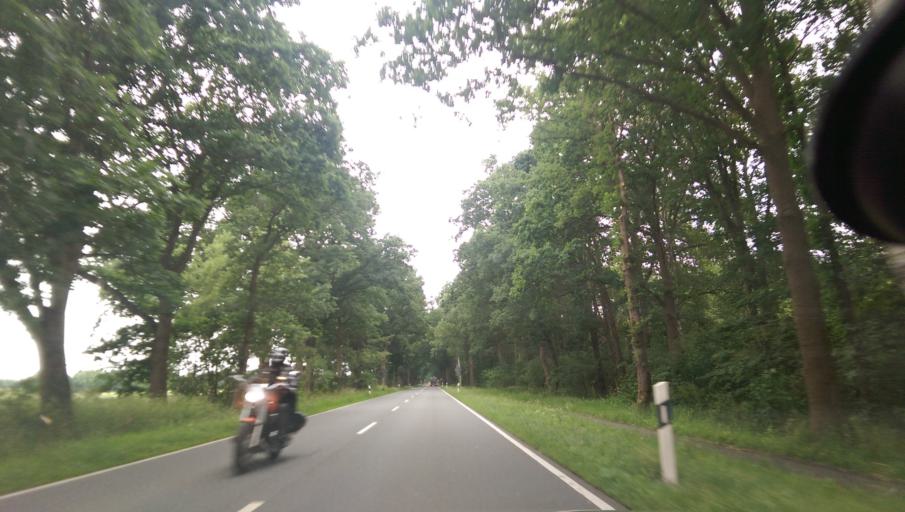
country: DE
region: Lower Saxony
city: Rotenburg
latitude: 53.0896
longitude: 9.4162
